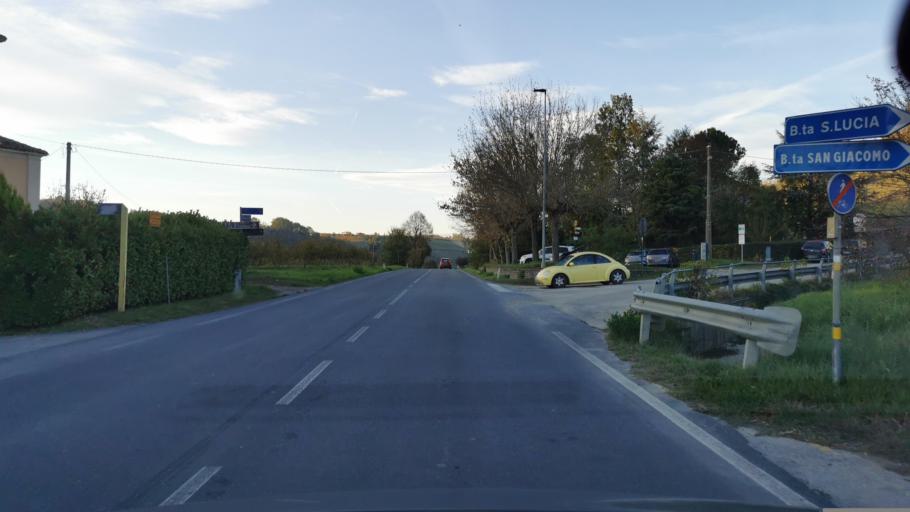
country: IT
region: Piedmont
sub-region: Provincia di Cuneo
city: Dogliani
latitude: 44.5430
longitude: 7.9277
